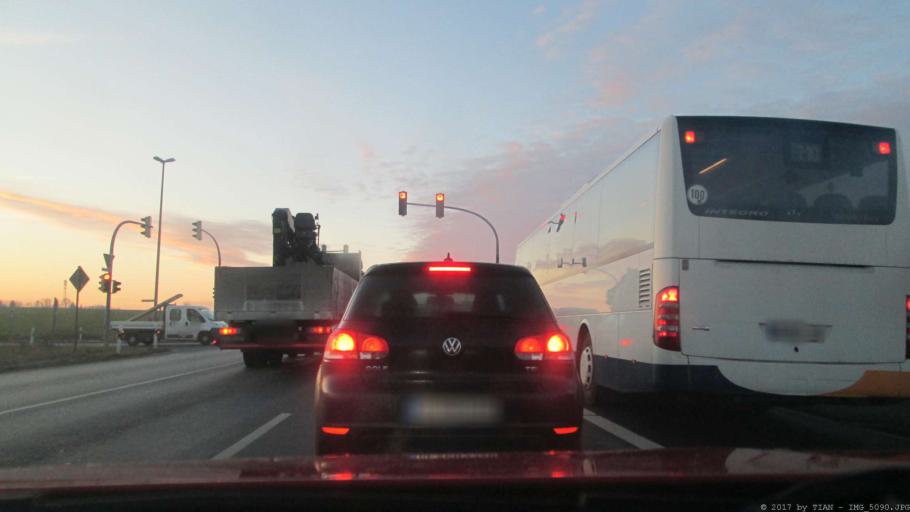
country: DE
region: Lower Saxony
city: Danndorf
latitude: 52.4260
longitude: 10.8476
